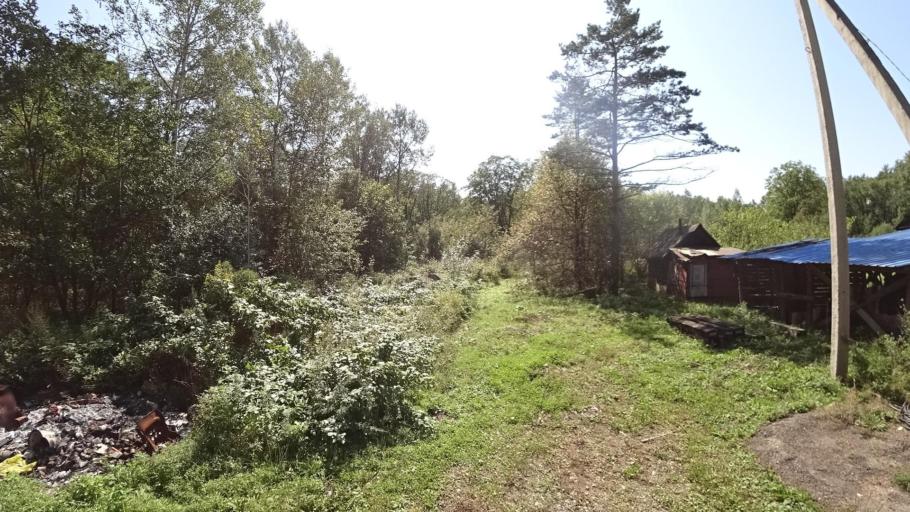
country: RU
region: Jewish Autonomous Oblast
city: Londoko
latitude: 49.0122
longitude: 132.2299
